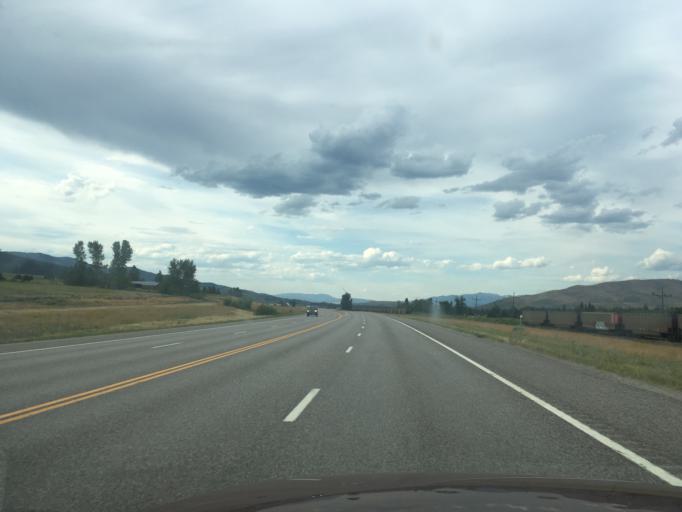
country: US
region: Montana
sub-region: Missoula County
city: Lolo
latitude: 46.6960
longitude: -114.0738
